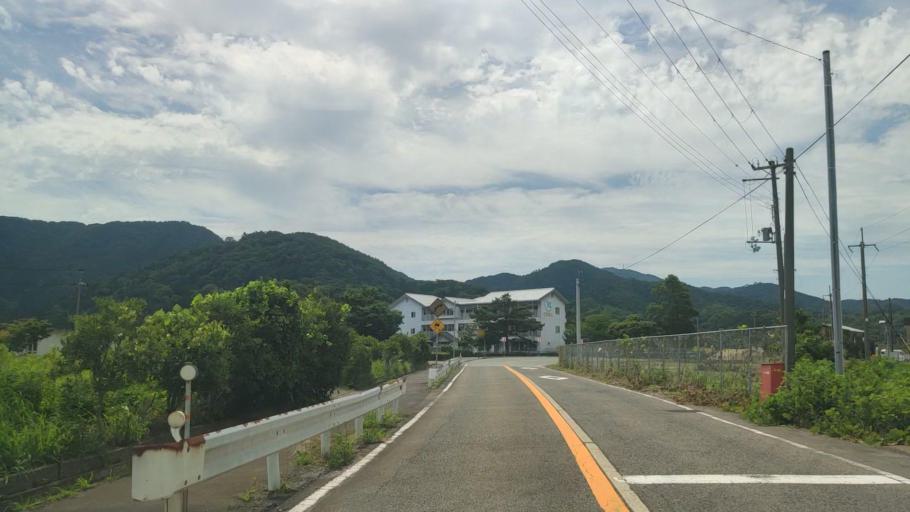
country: JP
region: Hyogo
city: Toyooka
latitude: 35.6476
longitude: 134.7581
